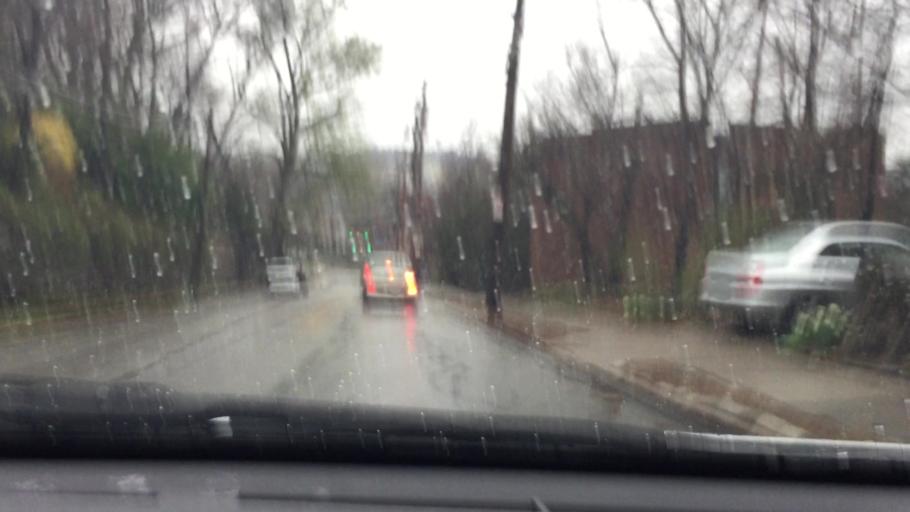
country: US
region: Pennsylvania
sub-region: Allegheny County
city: Bloomfield
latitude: 40.4473
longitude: -79.9354
